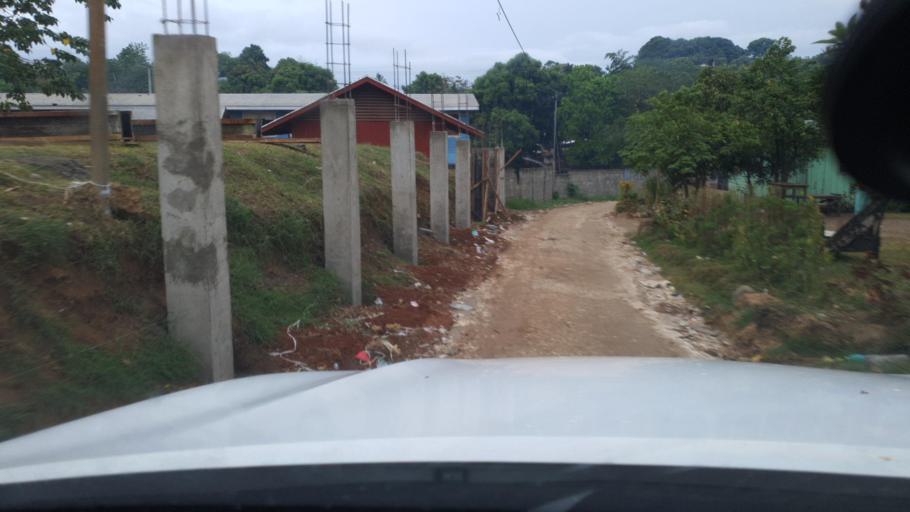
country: SB
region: Guadalcanal
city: Honiara
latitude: -9.4495
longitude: 159.9812
